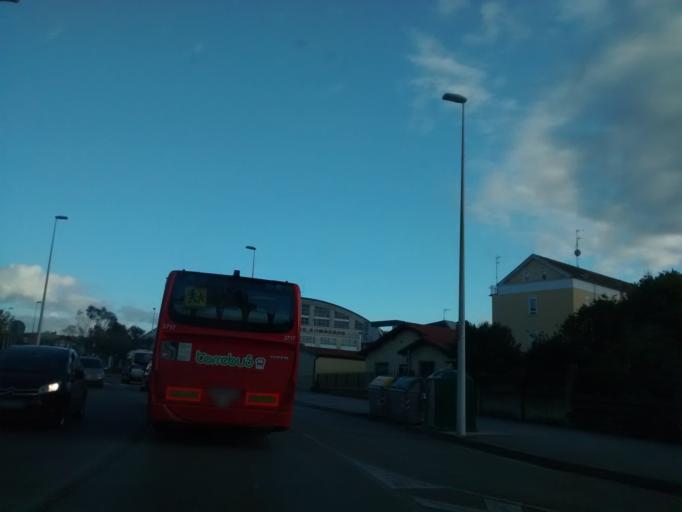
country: ES
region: Cantabria
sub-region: Provincia de Cantabria
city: Torrelavega
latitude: 43.3449
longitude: -4.0536
